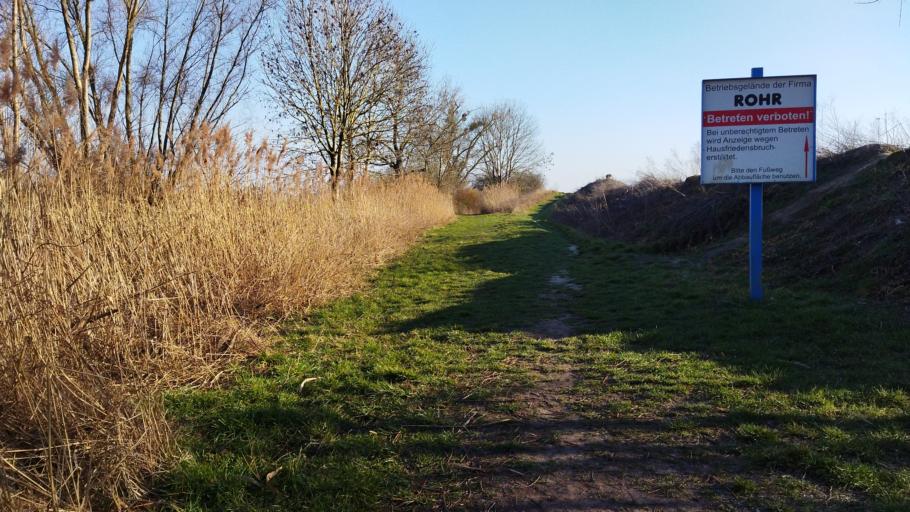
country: DE
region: Rheinland-Pfalz
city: Waldsee
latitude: 49.4132
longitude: 8.4508
